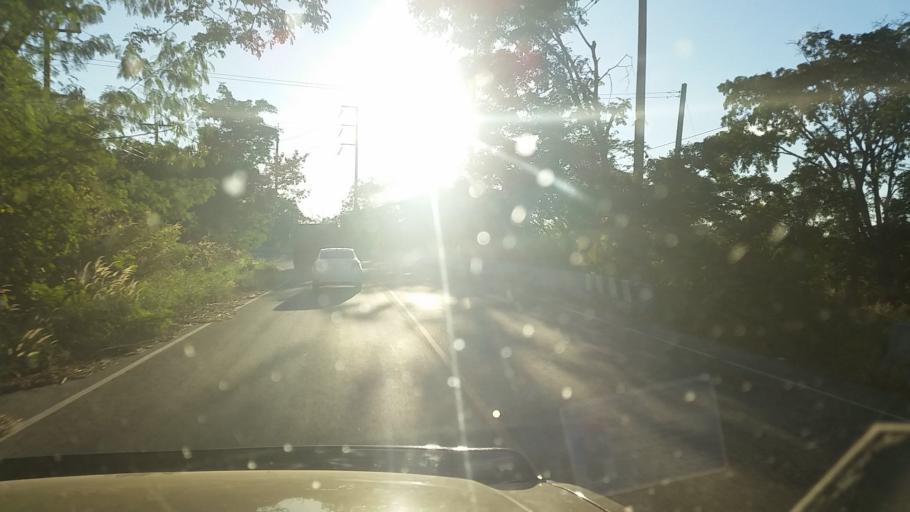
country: TH
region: Chaiyaphum
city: Sap Yai
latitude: 15.6800
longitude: 101.6916
